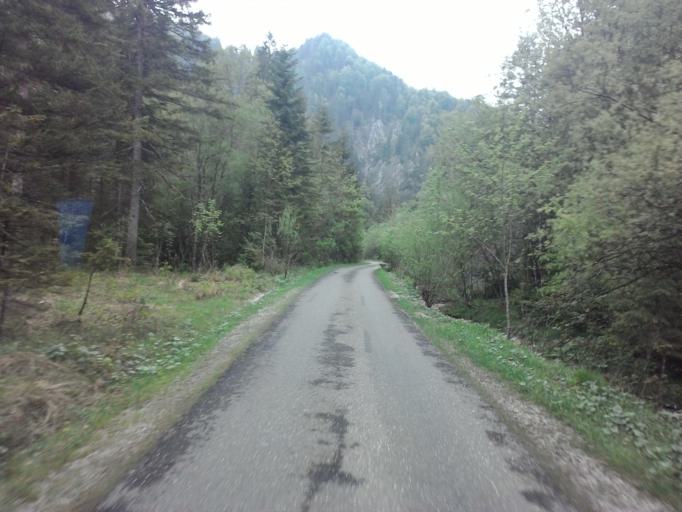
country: AT
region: Styria
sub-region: Politischer Bezirk Liezen
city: Wildalpen
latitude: 47.7023
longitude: 14.9998
